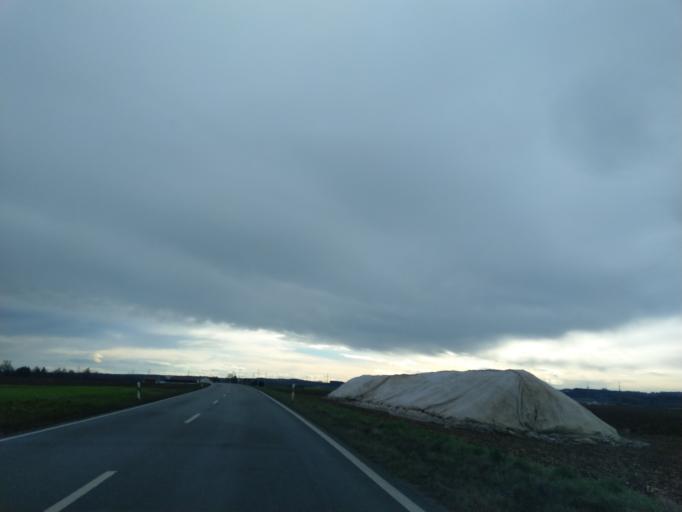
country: DE
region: Bavaria
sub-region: Lower Bavaria
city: Osterhofen
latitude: 48.6720
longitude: 13.0339
